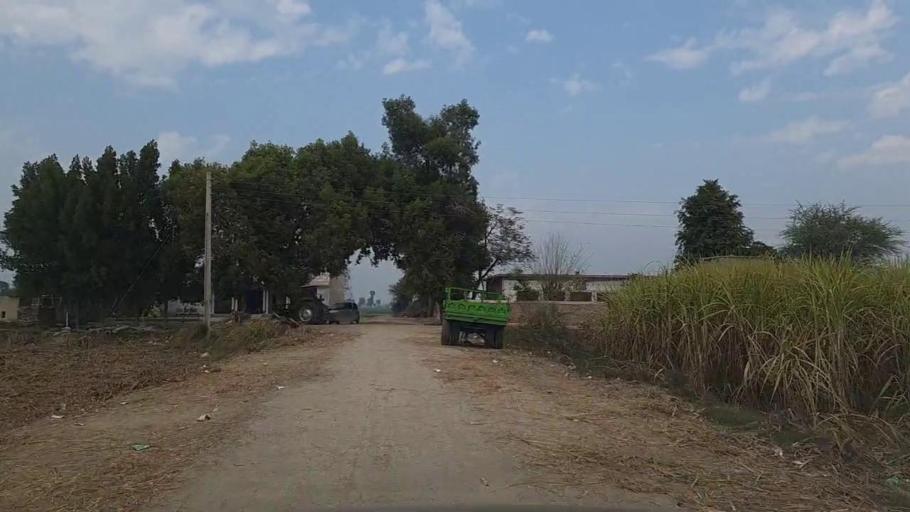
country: PK
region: Sindh
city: Daur
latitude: 26.3629
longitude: 68.3793
